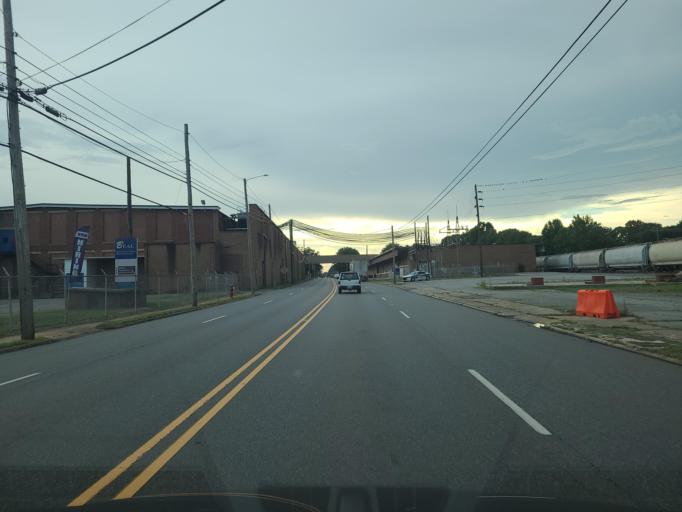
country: US
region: North Carolina
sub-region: Gaston County
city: Ranlo
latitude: 35.2789
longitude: -81.1283
